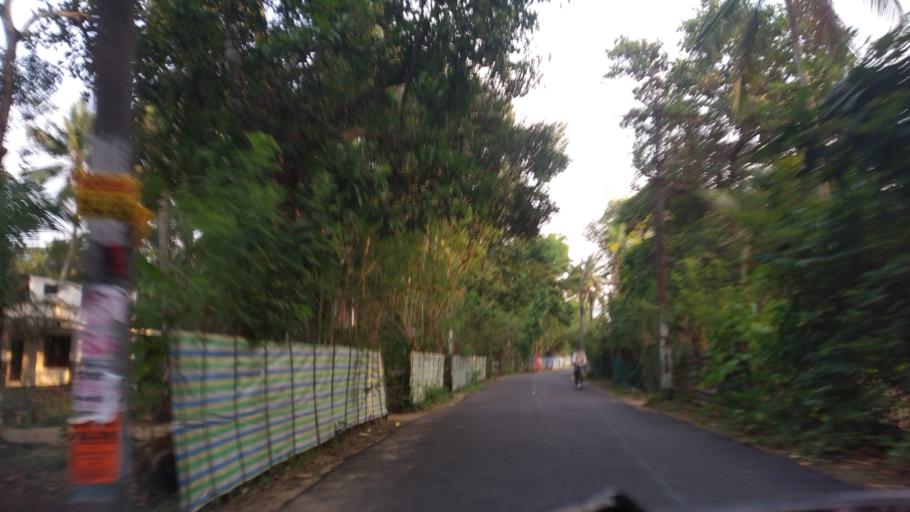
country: IN
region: Kerala
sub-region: Thrissur District
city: Thanniyam
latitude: 10.3551
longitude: 76.1120
